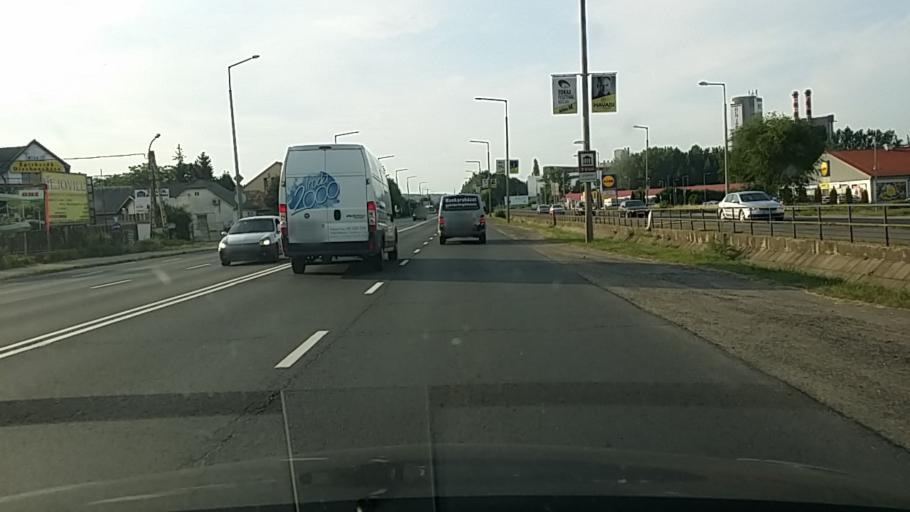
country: HU
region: Borsod-Abauj-Zemplen
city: Miskolc
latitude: 48.0582
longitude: 20.7965
